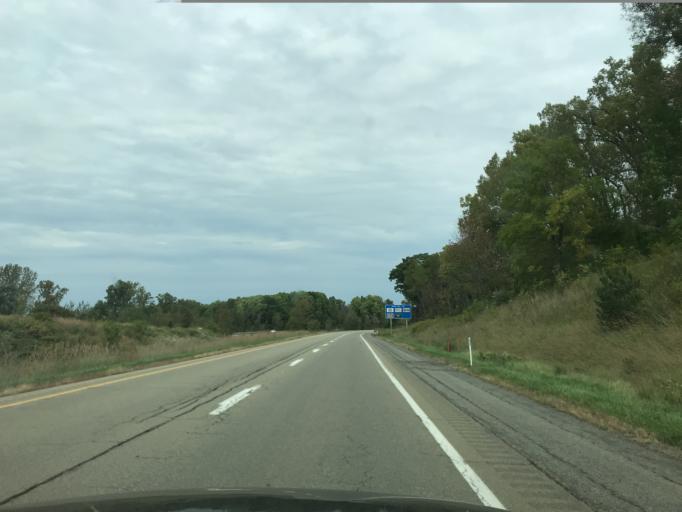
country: US
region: Pennsylvania
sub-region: Erie County
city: Erie
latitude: 42.0546
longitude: -80.1127
